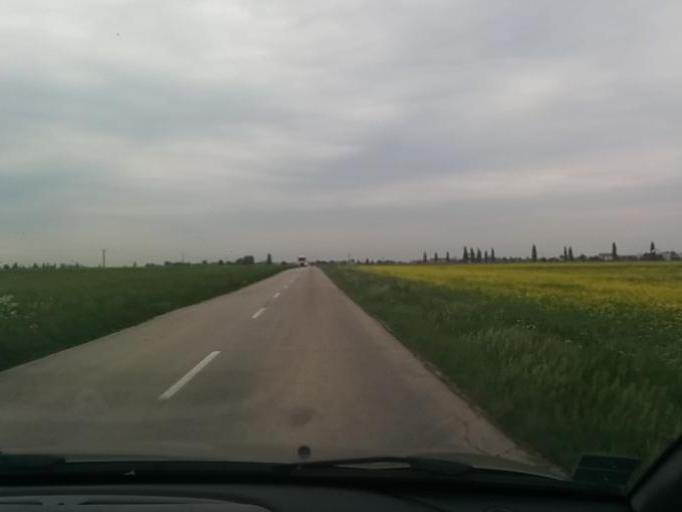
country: SK
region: Trnavsky
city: Sladkovicovo
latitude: 48.2100
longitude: 17.6155
